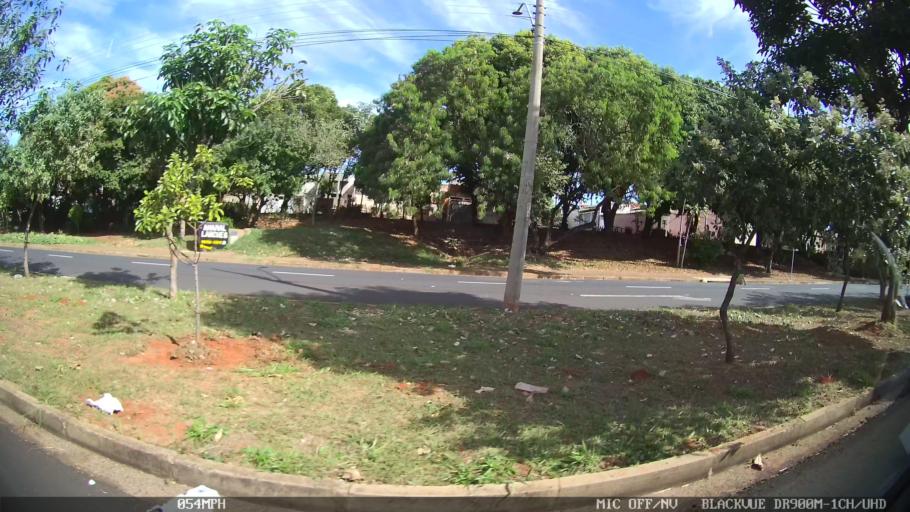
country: BR
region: Sao Paulo
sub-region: Sao Jose Do Rio Preto
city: Sao Jose do Rio Preto
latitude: -20.8342
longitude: -49.3479
